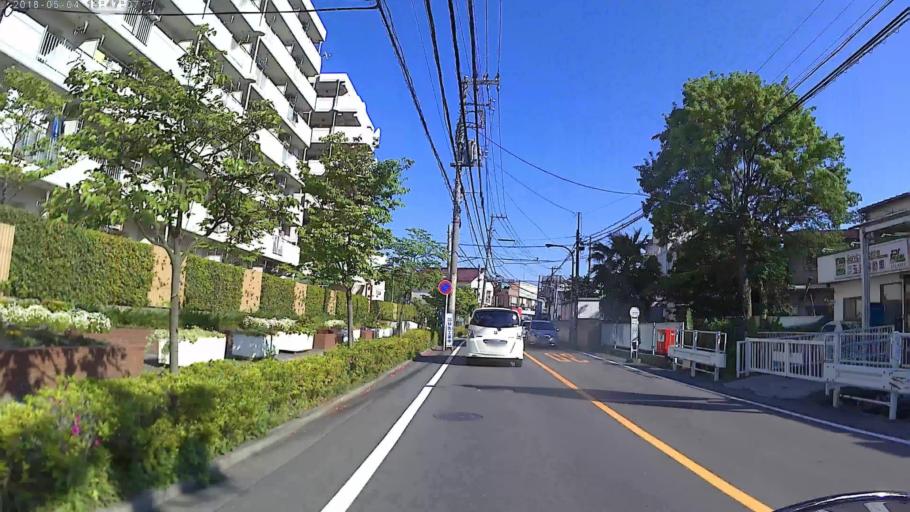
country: JP
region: Kanagawa
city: Yokohama
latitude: 35.4998
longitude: 139.6452
